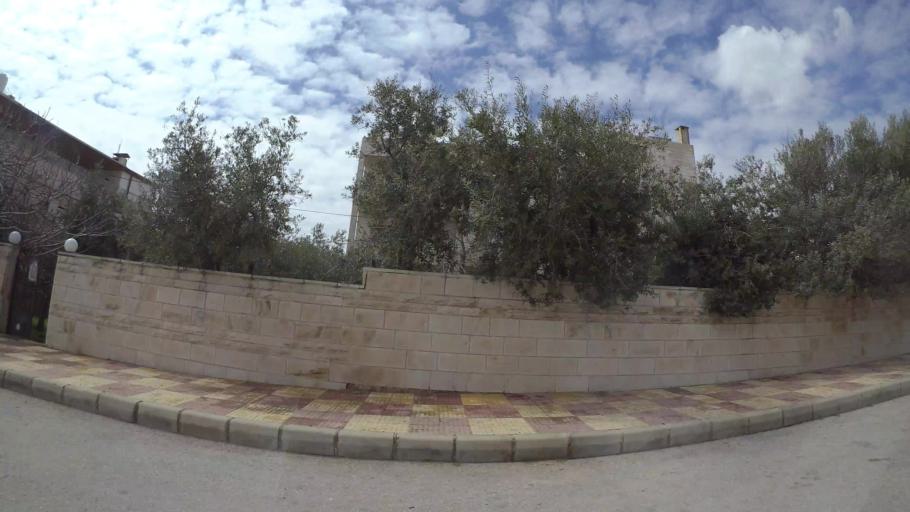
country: JO
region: Amman
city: Amman
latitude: 31.9967
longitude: 35.9105
